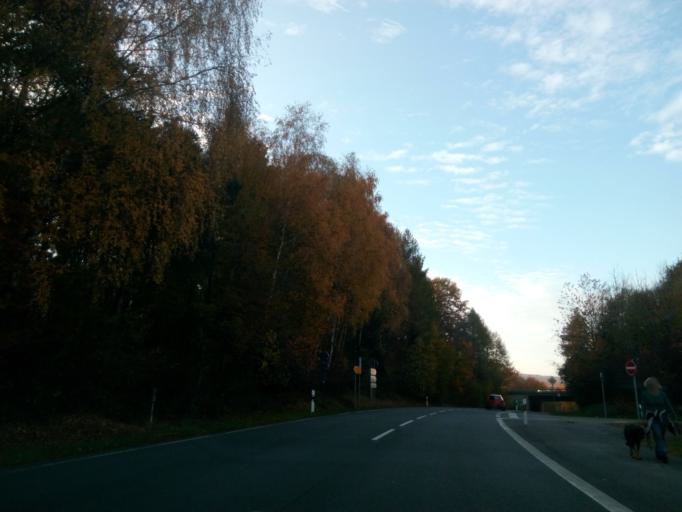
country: DE
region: Saarland
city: Sulzbach
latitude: 49.2823
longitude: 7.0164
